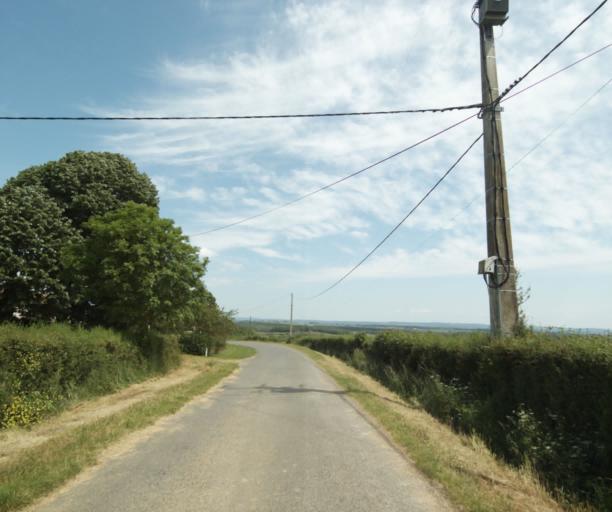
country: FR
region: Bourgogne
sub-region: Departement de Saone-et-Loire
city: Perrecy-les-Forges
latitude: 46.5975
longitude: 4.1481
